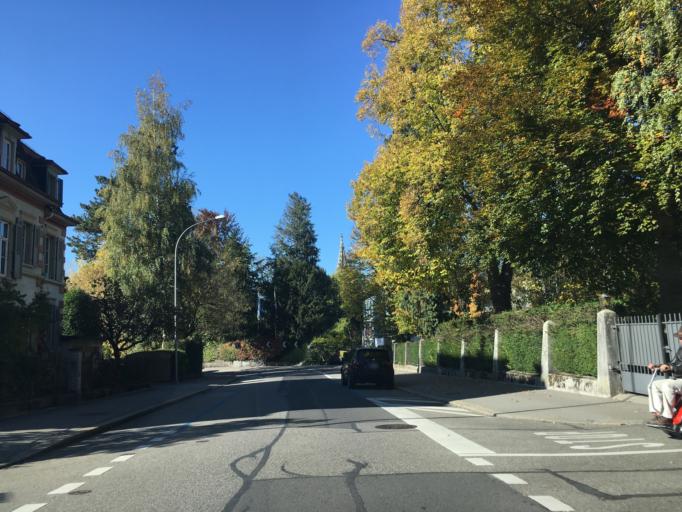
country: CH
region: Bern
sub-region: Bern-Mittelland District
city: Bern
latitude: 46.9433
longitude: 7.4552
